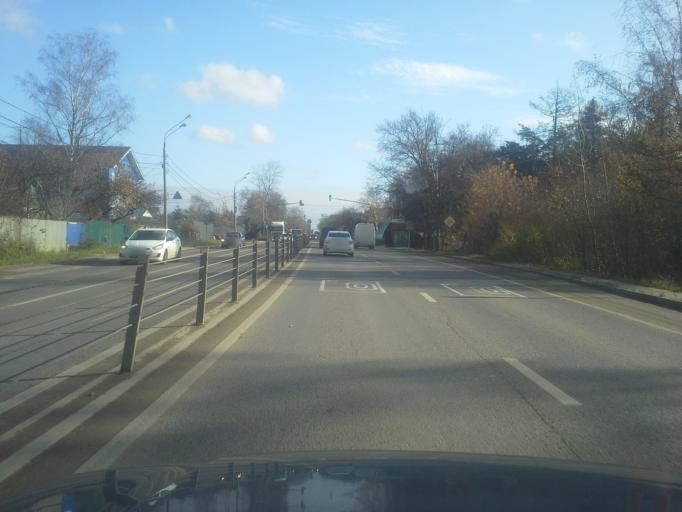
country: RU
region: Moskovskaya
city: Bol'shiye Vyazemy
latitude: 55.6298
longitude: 36.9931
